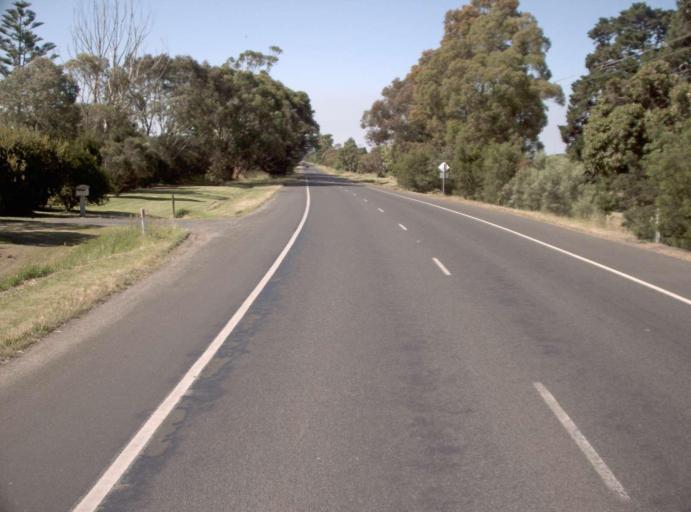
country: AU
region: Victoria
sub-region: Latrobe
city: Traralgon
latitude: -38.6029
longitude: 146.6671
